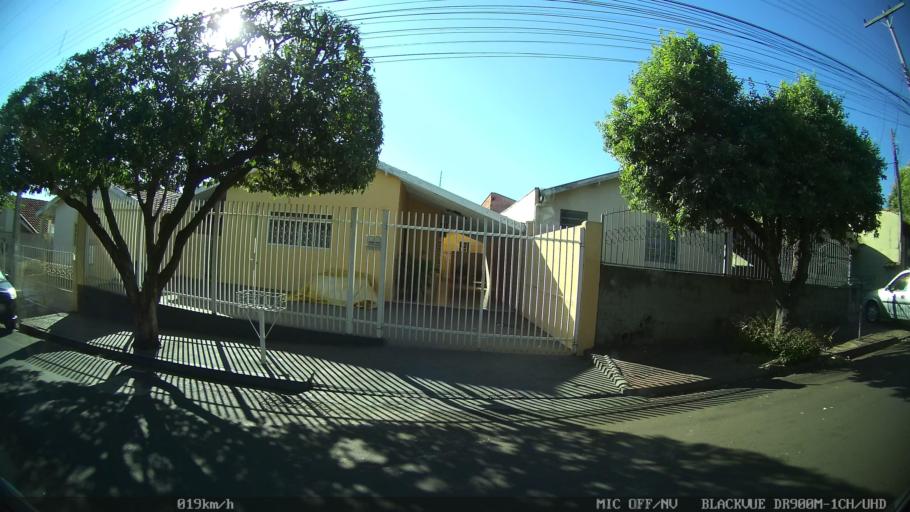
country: BR
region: Sao Paulo
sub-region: Olimpia
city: Olimpia
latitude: -20.7405
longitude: -48.9016
